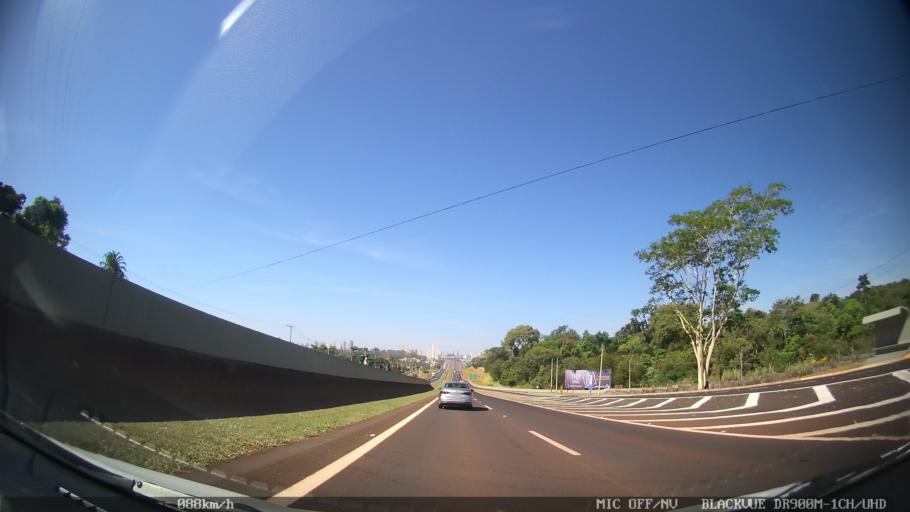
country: BR
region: Sao Paulo
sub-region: Ribeirao Preto
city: Ribeirao Preto
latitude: -21.2113
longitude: -47.8469
